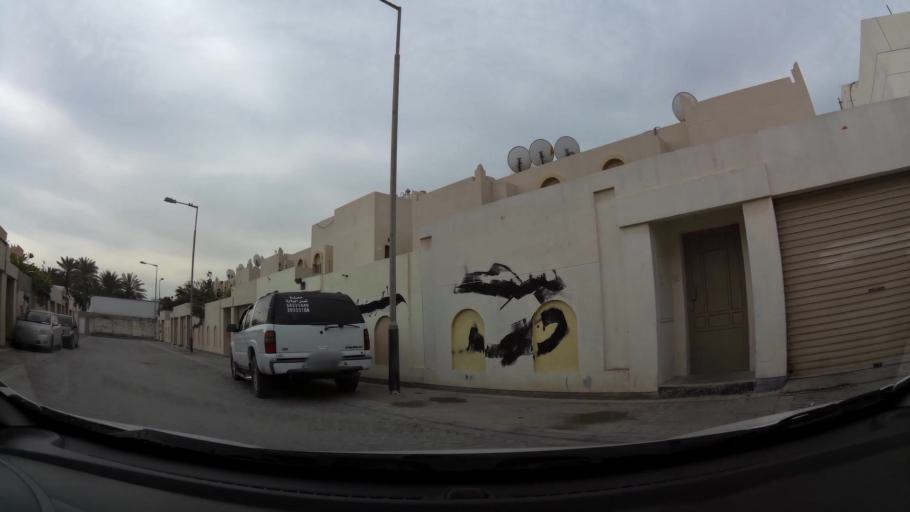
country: BH
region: Manama
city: Manama
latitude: 26.1819
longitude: 50.5814
